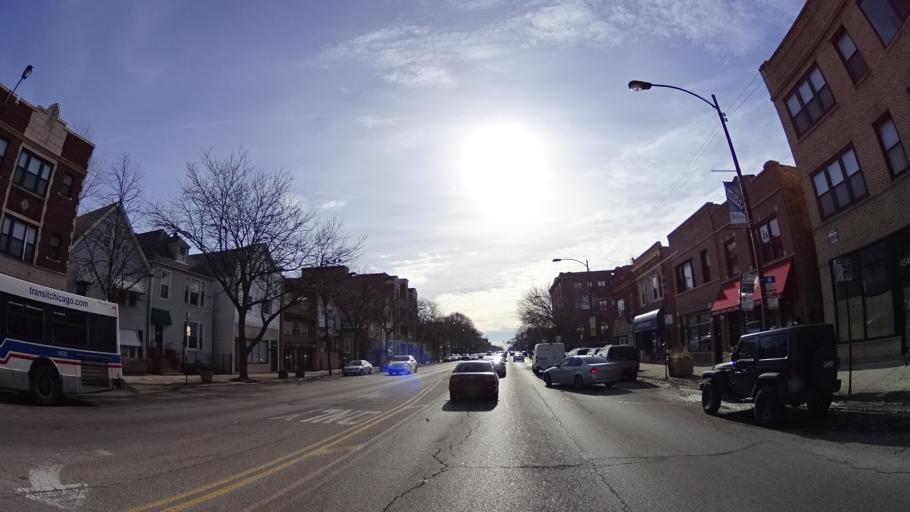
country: US
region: Illinois
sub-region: Cook County
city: Lincolnwood
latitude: 41.9649
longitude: -87.6889
